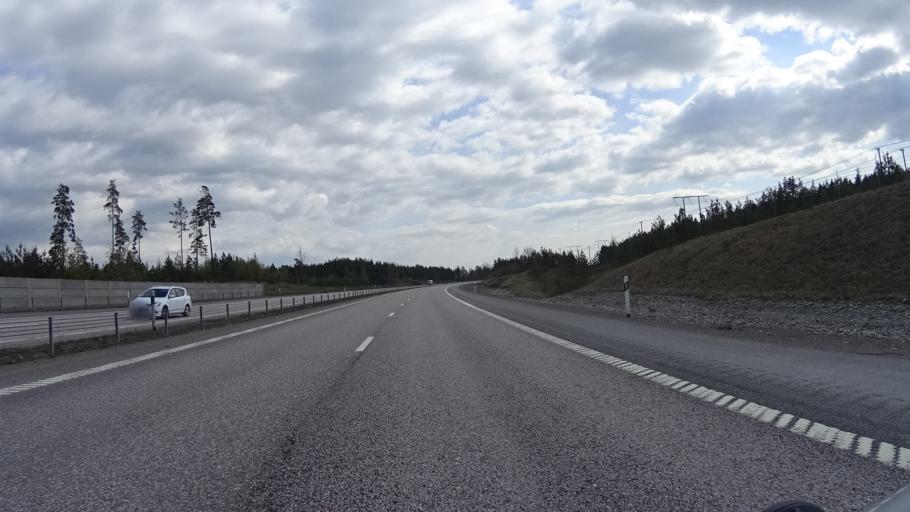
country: SE
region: Soedermanland
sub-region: Strangnas Kommun
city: Strangnas
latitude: 59.3533
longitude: 17.0050
